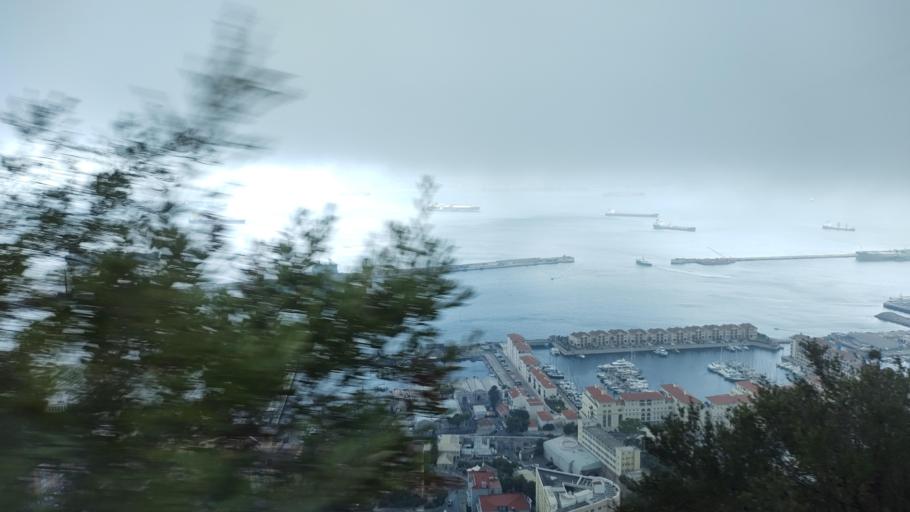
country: GI
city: Gibraltar
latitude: 36.1343
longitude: -5.3491
